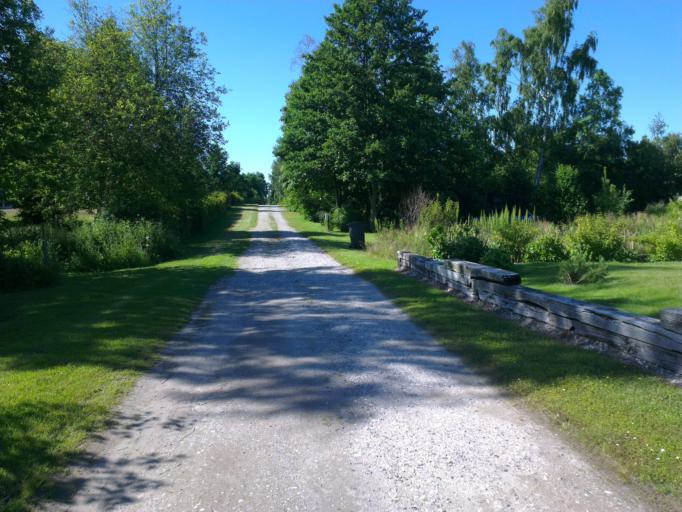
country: DK
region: Capital Region
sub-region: Frederikssund Kommune
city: Jaegerspris
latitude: 55.8174
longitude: 11.9411
